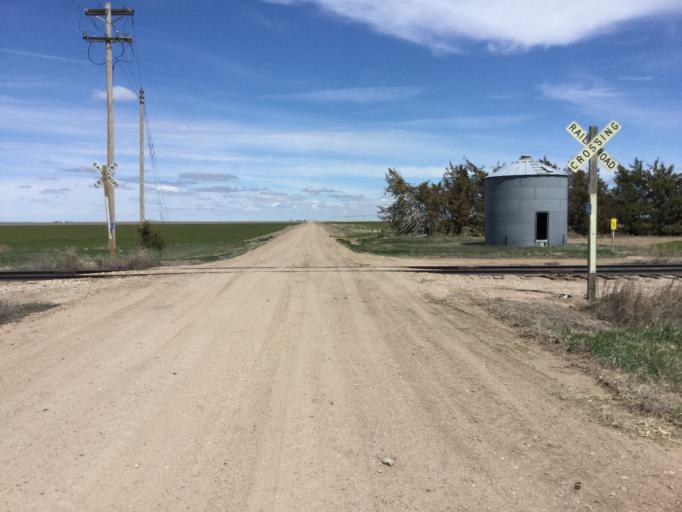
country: US
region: Kansas
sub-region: Sherman County
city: Goodland
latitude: 39.3400
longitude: -101.6329
